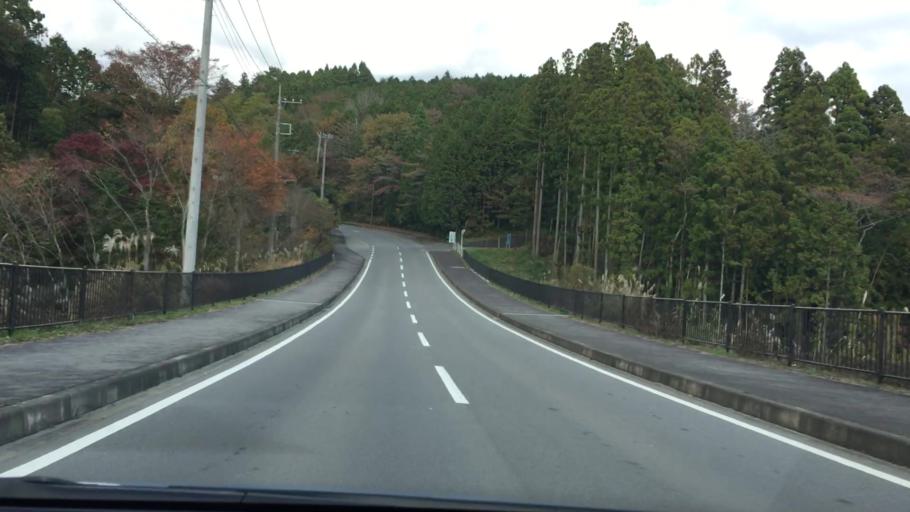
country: JP
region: Shizuoka
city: Gotemba
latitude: 35.3605
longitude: 138.9423
